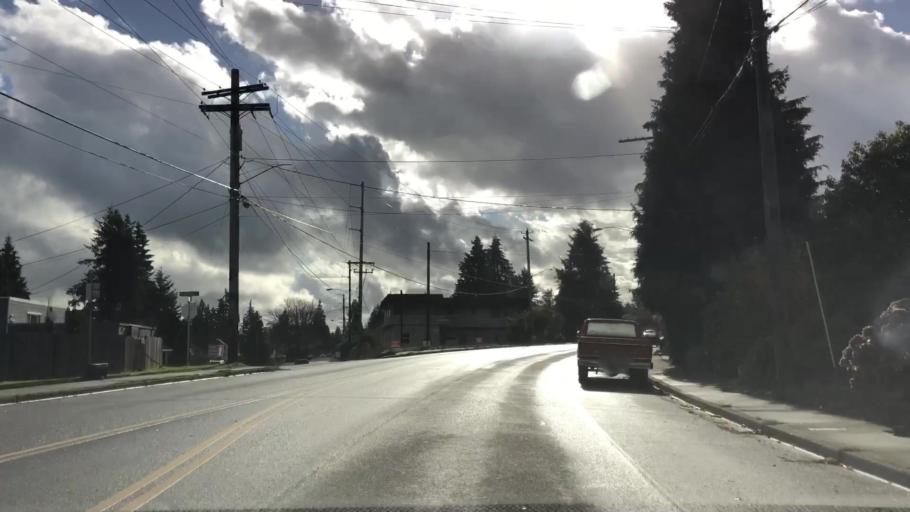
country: US
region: Washington
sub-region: Snohomish County
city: Everett
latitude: 47.9411
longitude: -122.2070
